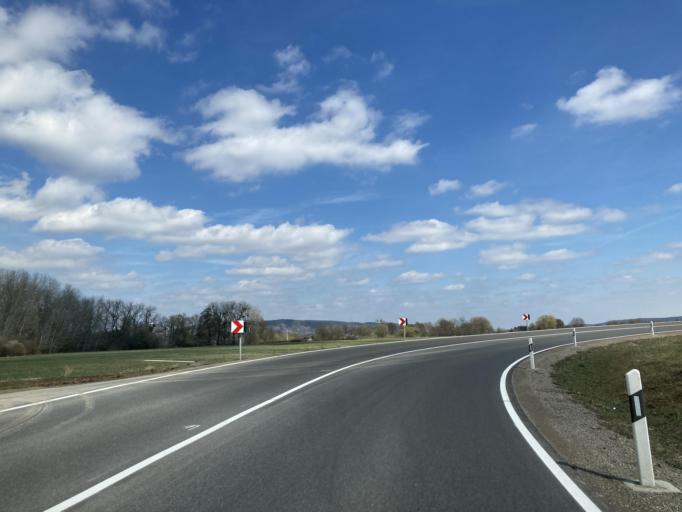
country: DE
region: Baden-Wuerttemberg
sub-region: Tuebingen Region
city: Rottenburg
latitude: 48.4755
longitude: 8.9586
